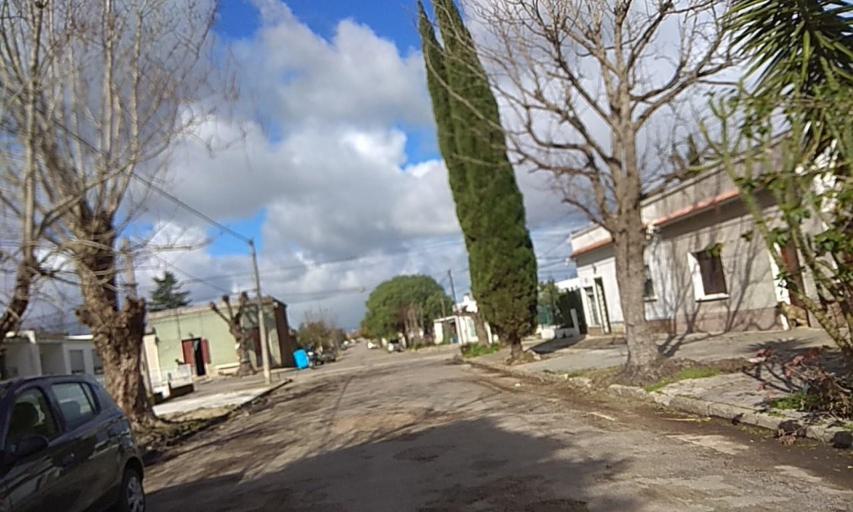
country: UY
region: Florida
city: Florida
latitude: -34.1040
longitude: -56.2194
